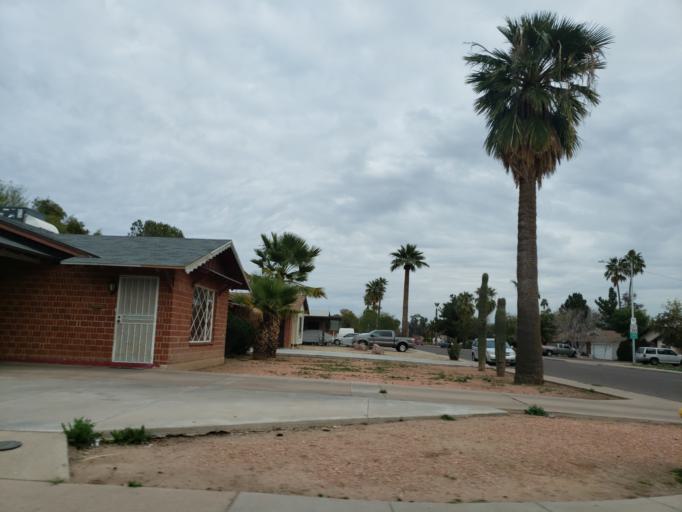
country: US
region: Arizona
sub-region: Maricopa County
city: Glendale
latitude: 33.5314
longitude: -112.1385
